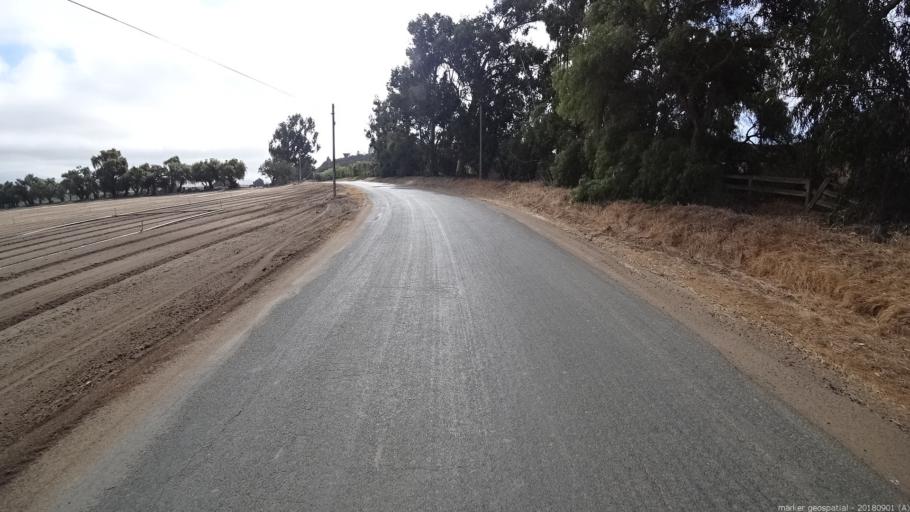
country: US
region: California
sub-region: Monterey County
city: Soledad
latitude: 36.3818
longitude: -121.3533
